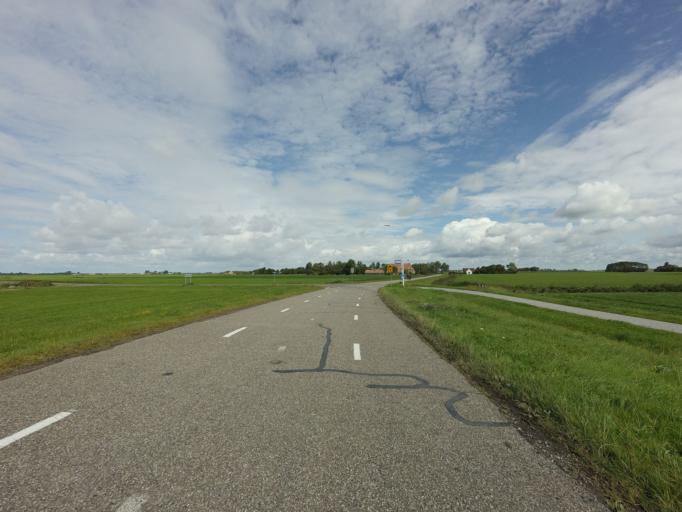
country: NL
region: Friesland
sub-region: Sudwest Fryslan
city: Makkum
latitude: 53.0959
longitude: 5.4197
